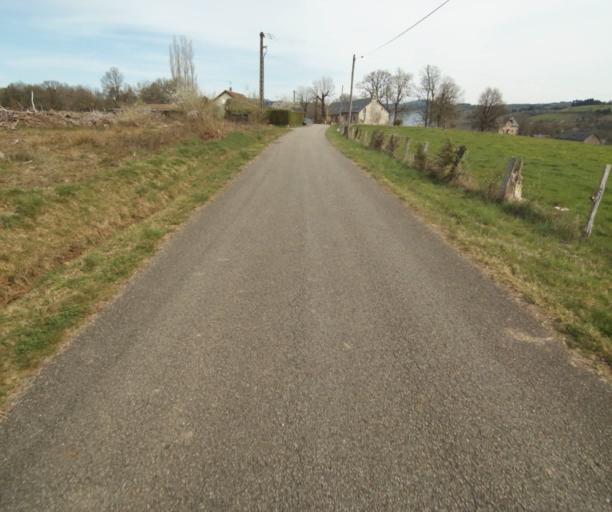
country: FR
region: Limousin
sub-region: Departement de la Correze
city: Correze
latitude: 45.3684
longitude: 1.8194
